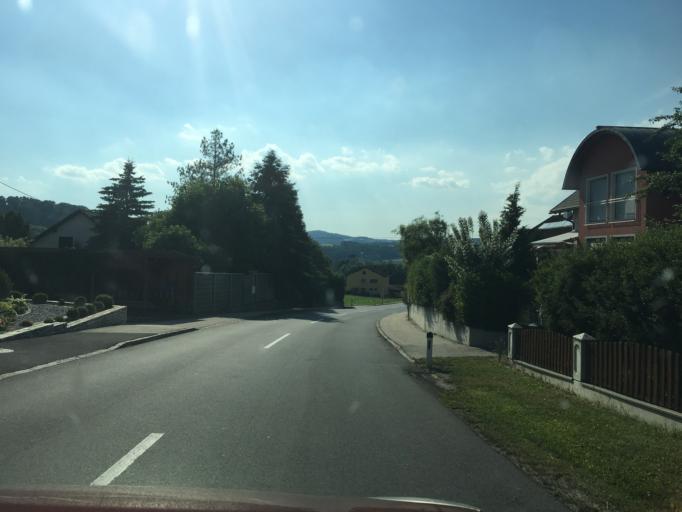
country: AT
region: Upper Austria
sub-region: Politischer Bezirk Linz-Land
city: Enns
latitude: 48.2863
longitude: 14.4888
